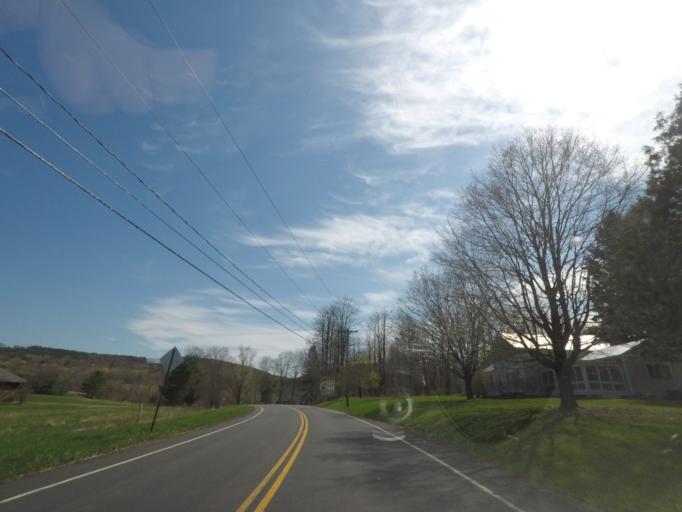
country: US
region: New York
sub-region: Columbia County
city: Chatham
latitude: 42.3856
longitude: -73.5309
